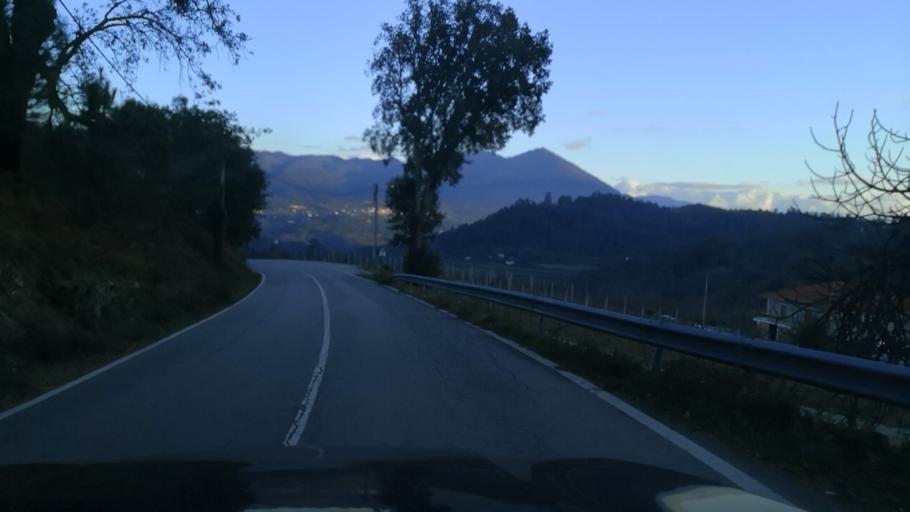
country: PT
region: Vila Real
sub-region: Mondim de Basto
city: Mondim de Basto
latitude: 41.4615
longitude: -7.9595
